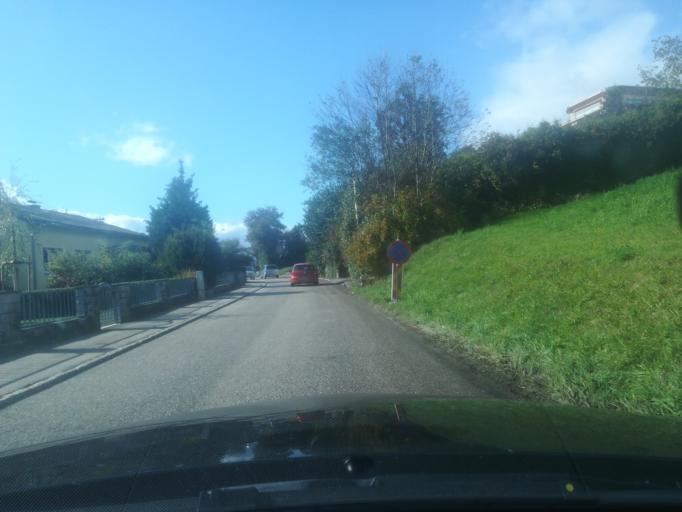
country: AT
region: Upper Austria
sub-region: Politischer Bezirk Urfahr-Umgebung
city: Eidenberg
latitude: 48.3584
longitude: 14.2619
